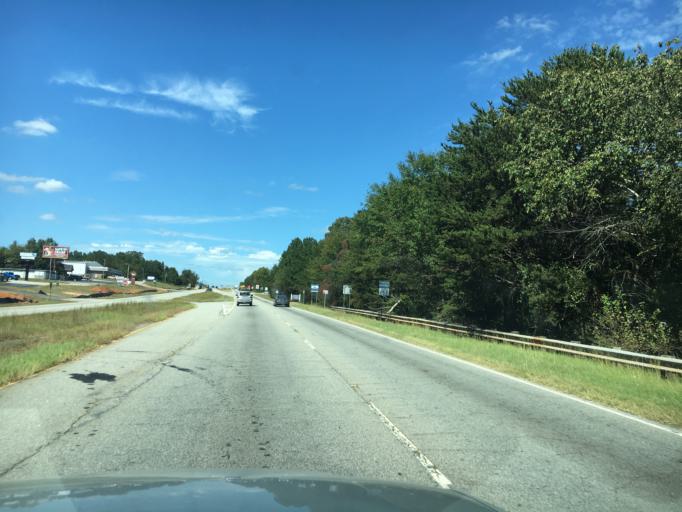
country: US
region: South Carolina
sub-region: Anderson County
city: Powdersville
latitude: 34.8066
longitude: -82.5126
